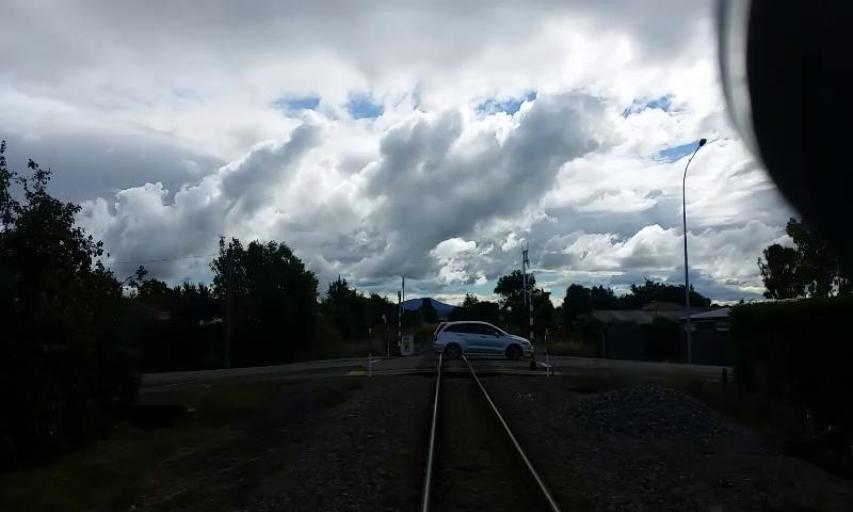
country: NZ
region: Canterbury
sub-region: Waimakariri District
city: Woodend
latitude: -43.3106
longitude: 172.6001
